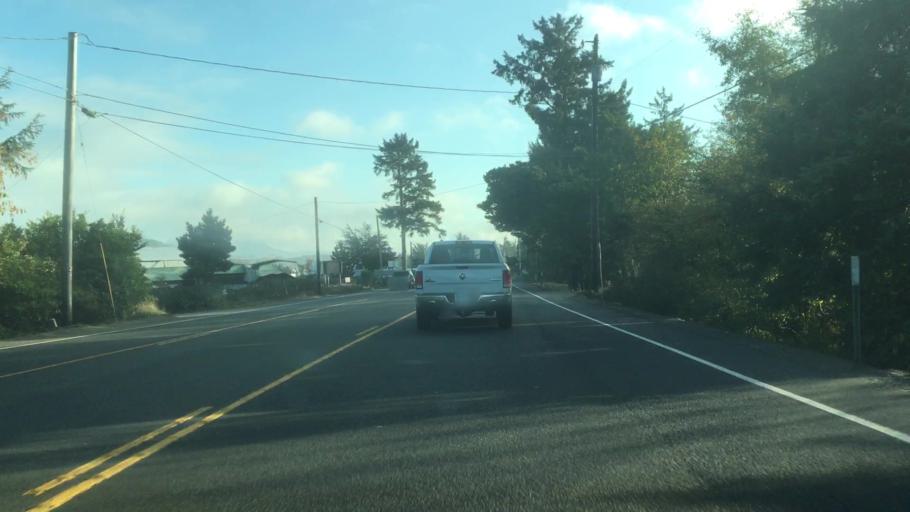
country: US
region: Oregon
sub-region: Clatsop County
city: Gearhart
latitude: 46.0224
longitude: -123.9115
